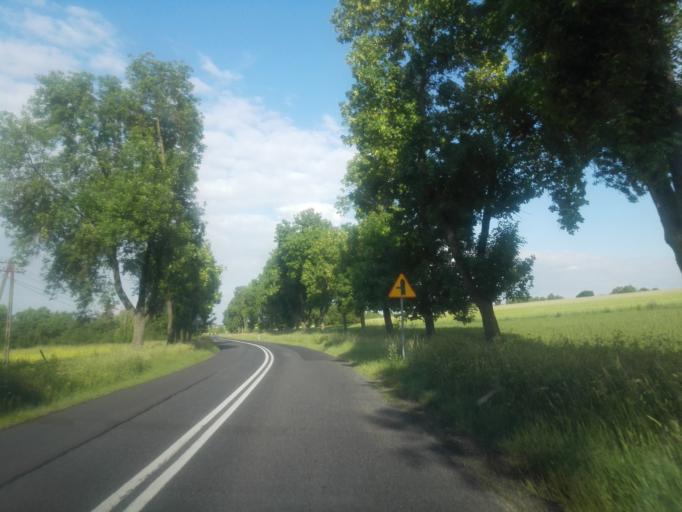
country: PL
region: Silesian Voivodeship
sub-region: Powiat czestochowski
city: Potok Zloty
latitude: 50.7360
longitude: 19.3840
